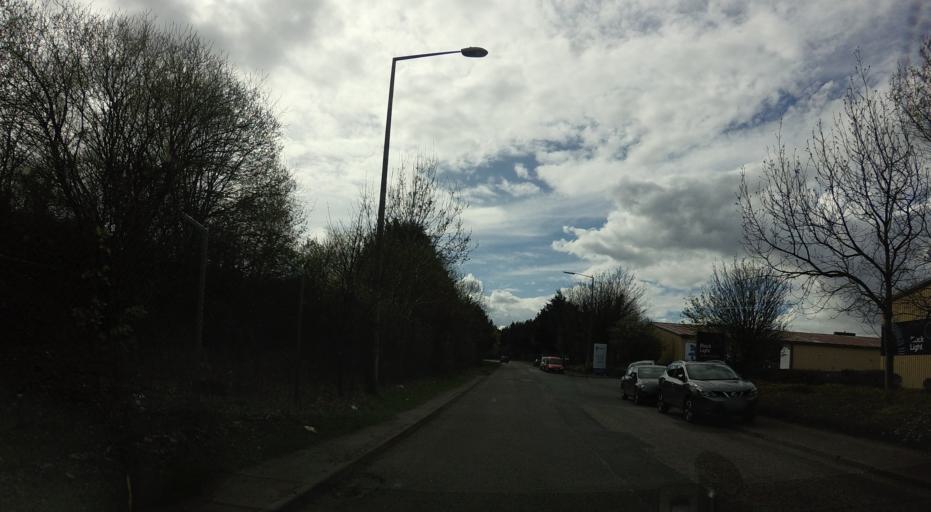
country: GB
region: Scotland
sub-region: Edinburgh
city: Edinburgh
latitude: 55.9823
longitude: -3.2481
